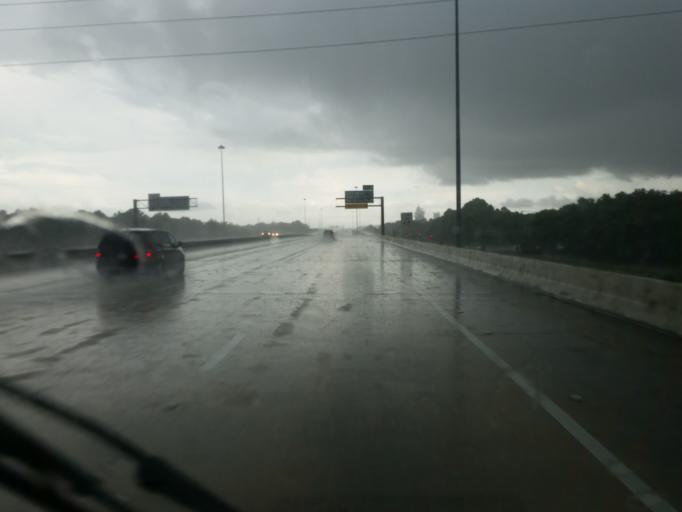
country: US
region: Alabama
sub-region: Mobile County
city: Prichard
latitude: 30.7338
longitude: -88.0803
